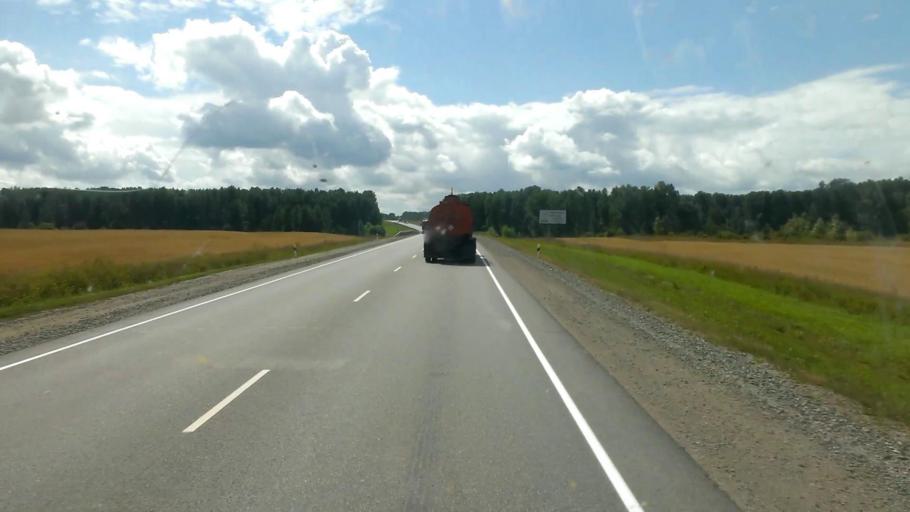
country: RU
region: Altai Krai
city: Troitskoye
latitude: 52.9862
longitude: 84.7436
